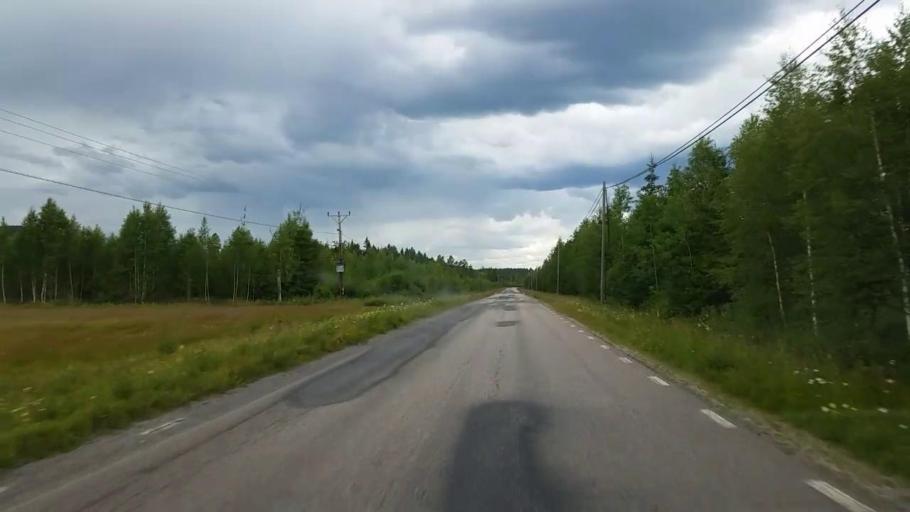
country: SE
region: Gaevleborg
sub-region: Ovanakers Kommun
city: Edsbyn
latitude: 61.4469
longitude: 15.8841
